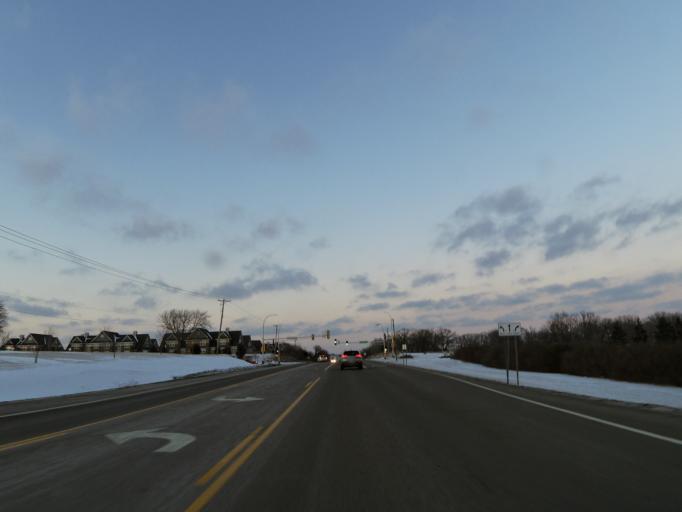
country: US
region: Minnesota
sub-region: Dakota County
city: Rosemount
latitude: 44.7489
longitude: -93.1254
